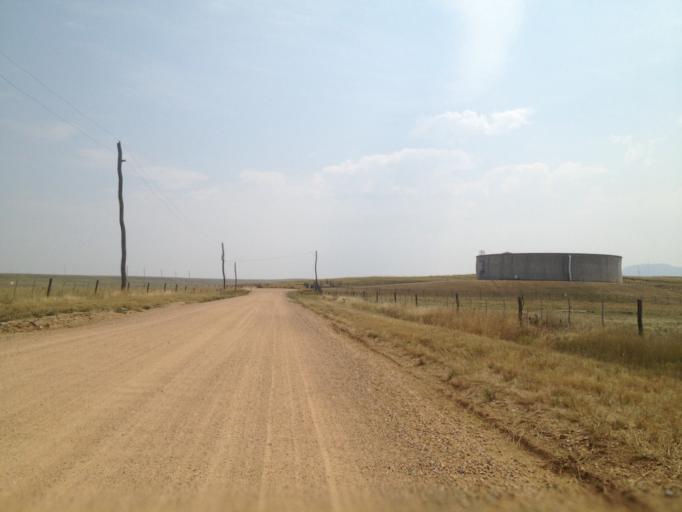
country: US
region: Colorado
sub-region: Boulder County
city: Superior
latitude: 39.9416
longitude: -105.1988
